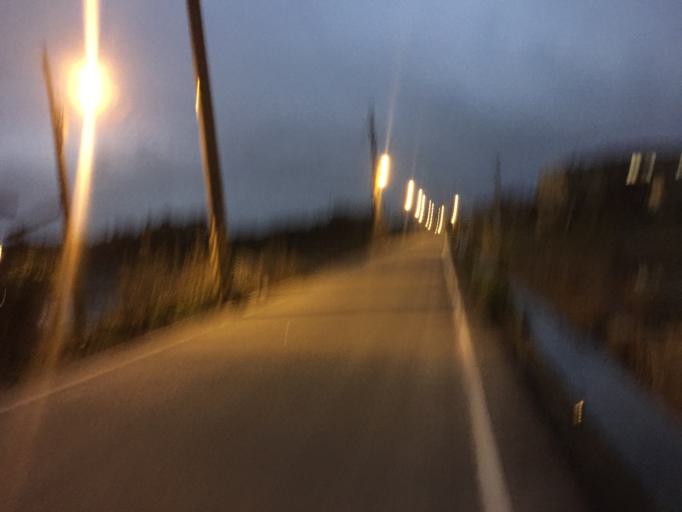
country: TW
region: Taiwan
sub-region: Yilan
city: Yilan
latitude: 24.6583
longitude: 121.7839
